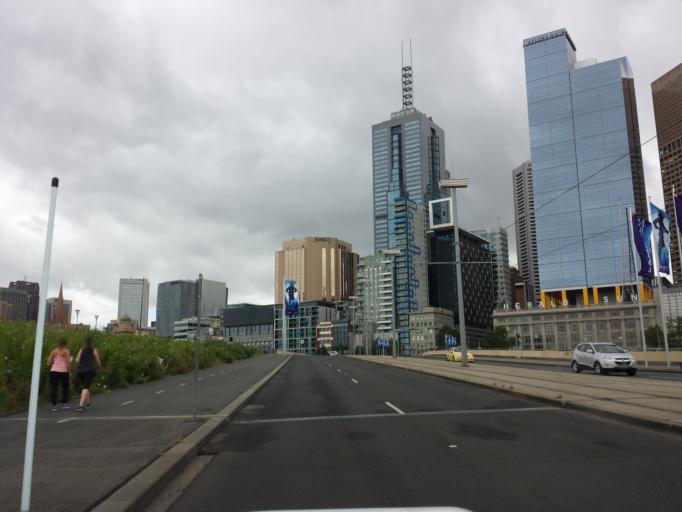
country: AU
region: Victoria
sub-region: Melbourne
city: Southbank
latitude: -37.8179
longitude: 144.9747
